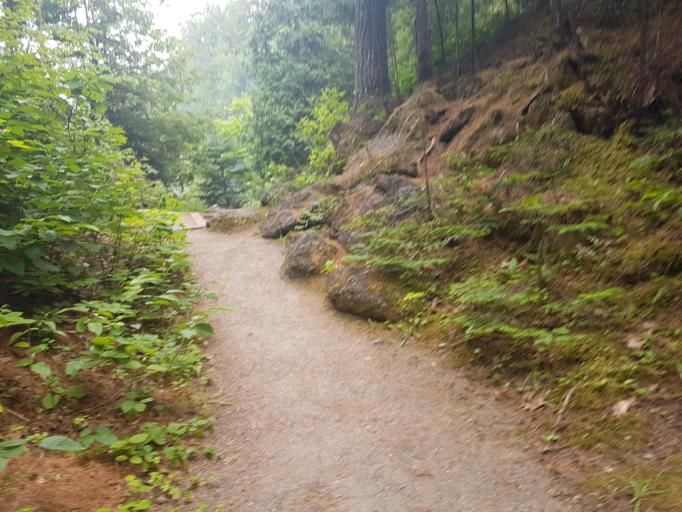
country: CA
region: Quebec
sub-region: Outaouais
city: Fort-Coulonge
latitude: 45.8743
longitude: -76.6874
